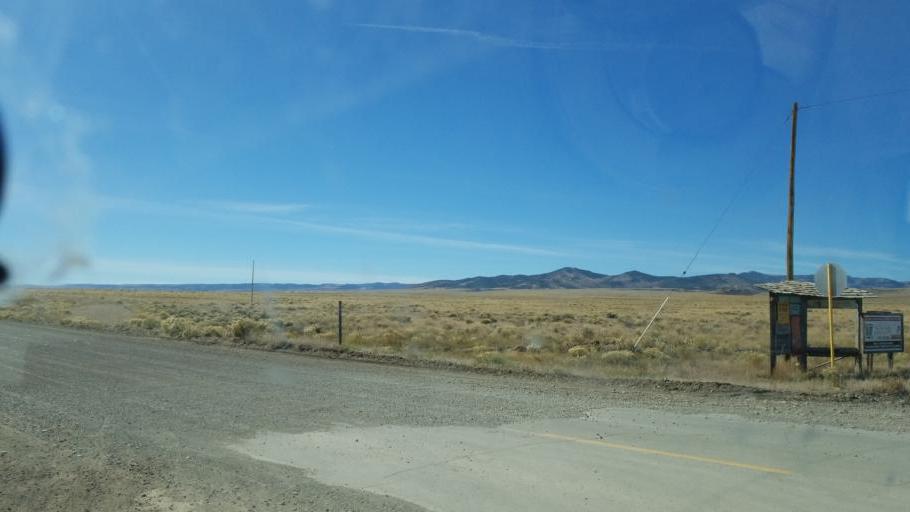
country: US
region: Colorado
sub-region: Rio Grande County
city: Monte Vista
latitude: 37.4011
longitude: -106.1488
